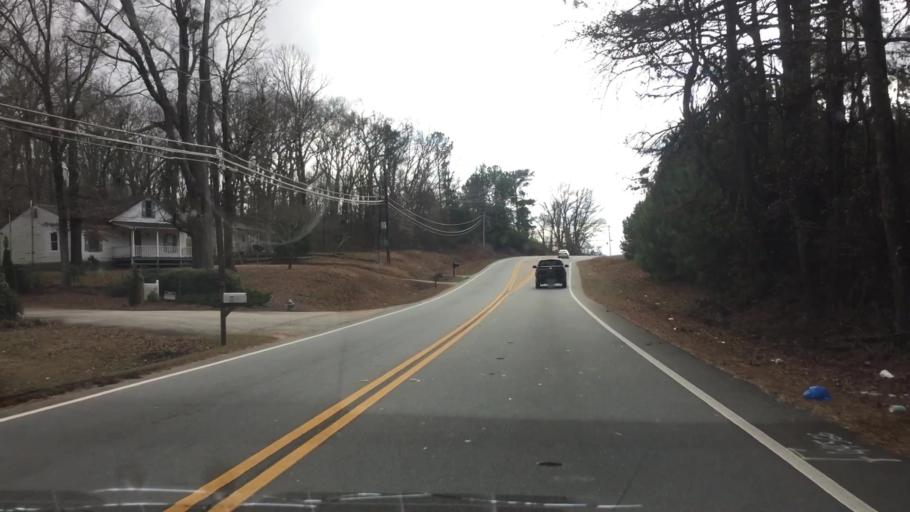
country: US
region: Georgia
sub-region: Henry County
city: McDonough
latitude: 33.4393
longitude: -84.1565
